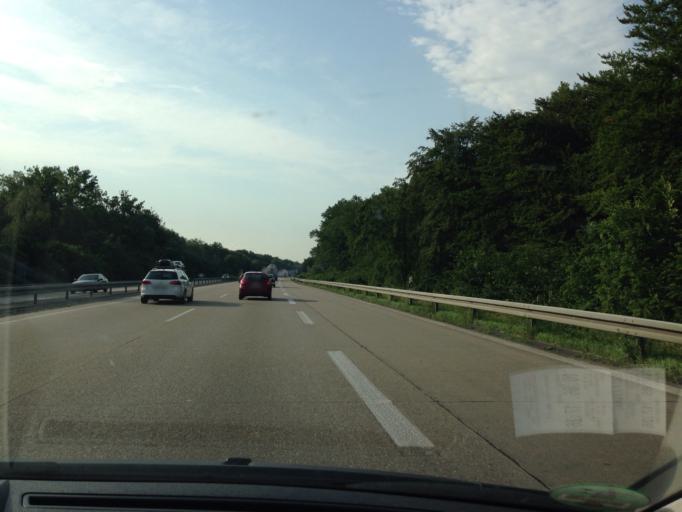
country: DE
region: North Rhine-Westphalia
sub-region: Regierungsbezirk Munster
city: Ascheberg
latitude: 51.8436
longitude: 7.5845
